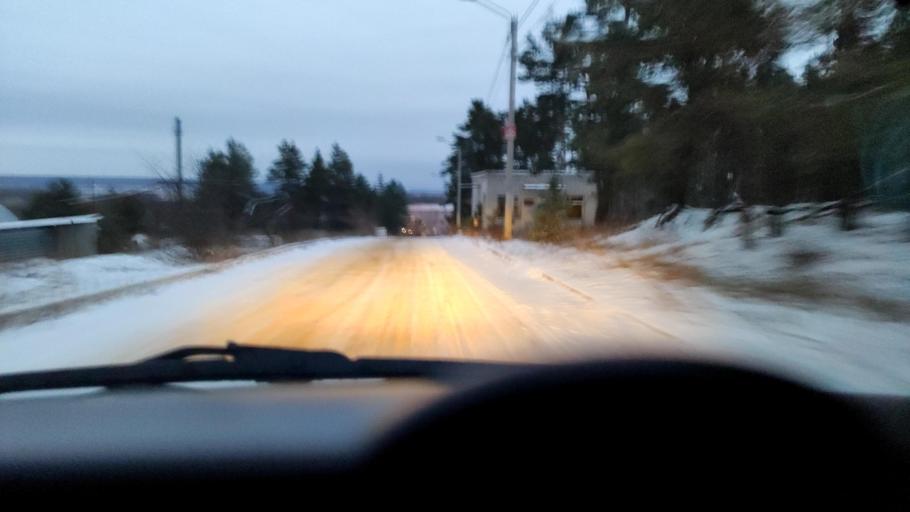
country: RU
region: Voronezj
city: Pridonskoy
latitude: 51.7024
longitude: 39.1059
